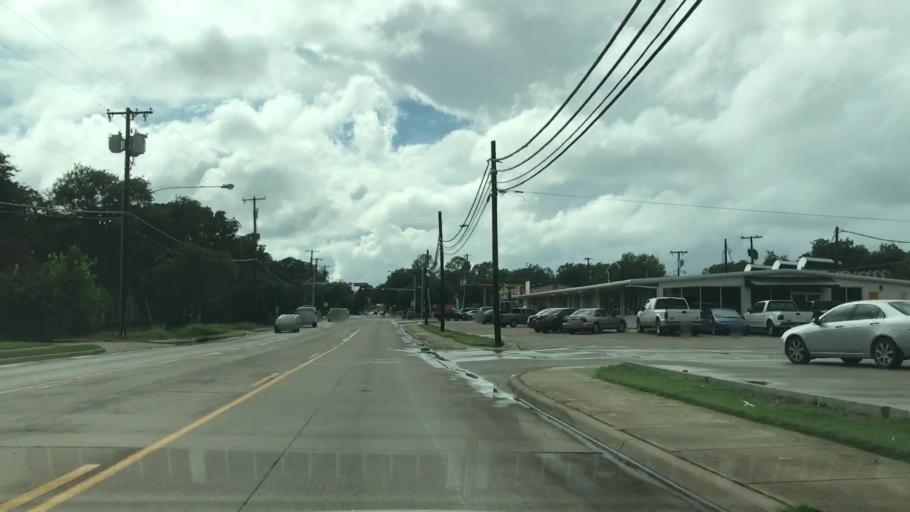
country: US
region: Texas
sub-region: Dallas County
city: Irving
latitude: 32.8297
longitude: -96.9286
